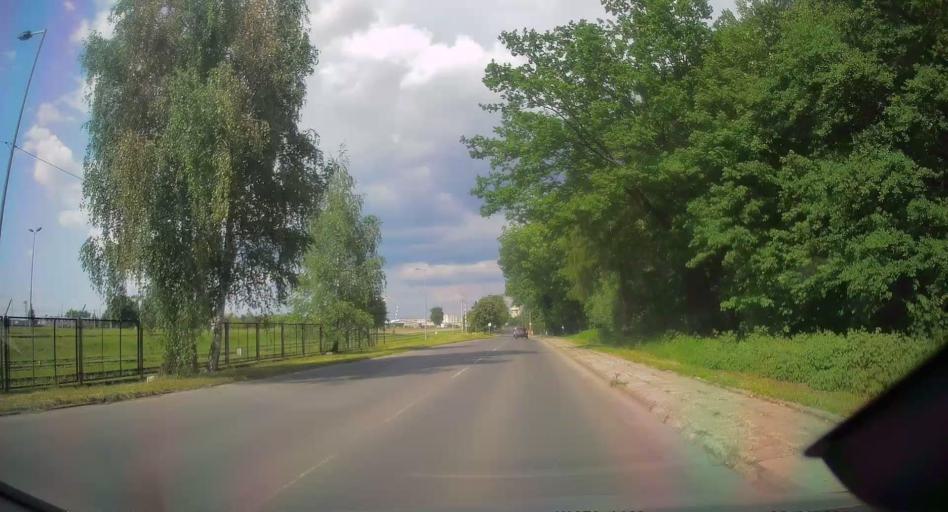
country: PL
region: Subcarpathian Voivodeship
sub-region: Powiat debicki
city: Debica
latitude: 50.0473
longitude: 21.3927
